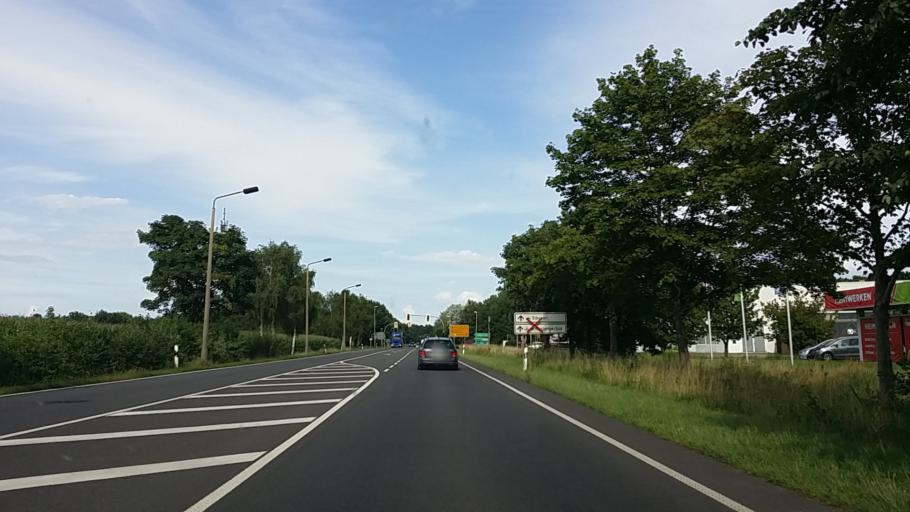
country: DE
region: Brandenburg
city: Wittenberge
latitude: 53.0181
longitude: 11.7402
